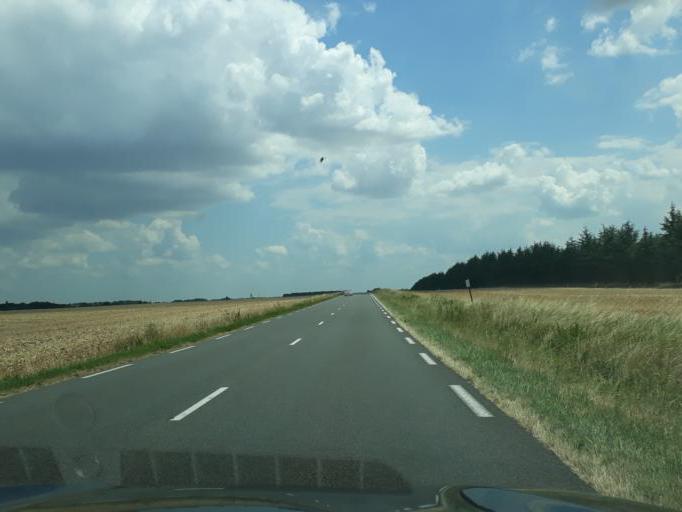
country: FR
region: Centre
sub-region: Departement du Cher
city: Avord
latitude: 47.0381
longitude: 2.5965
